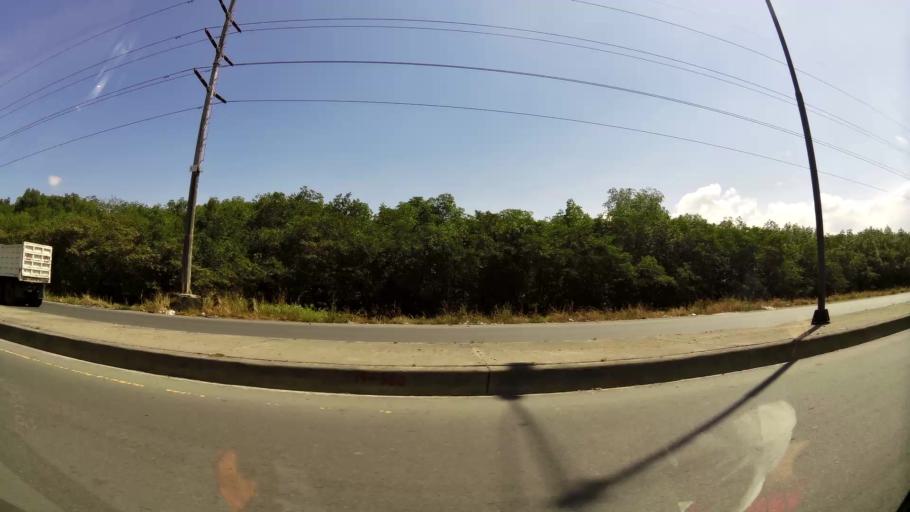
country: EC
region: Guayas
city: Guayaquil
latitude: -2.2154
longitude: -79.9564
